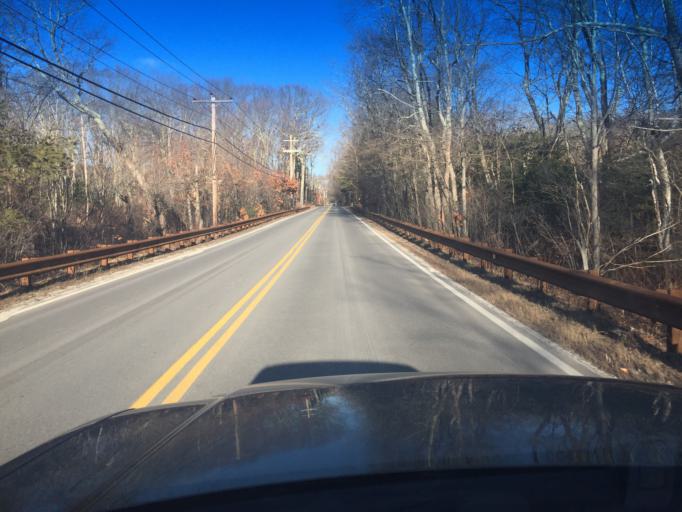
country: US
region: Massachusetts
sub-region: Middlesex County
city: Sherborn
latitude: 42.2246
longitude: -71.3945
